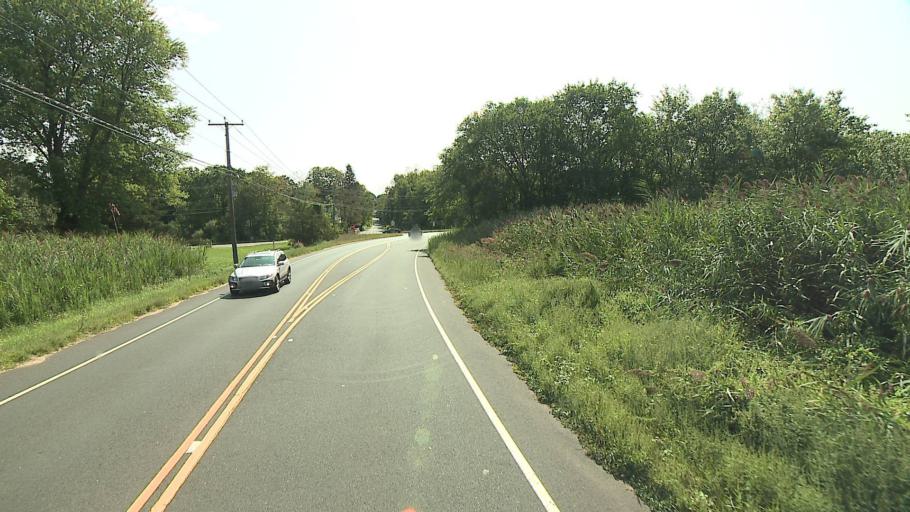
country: US
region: Connecticut
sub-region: Fairfield County
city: Newtown
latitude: 41.4366
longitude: -73.3582
